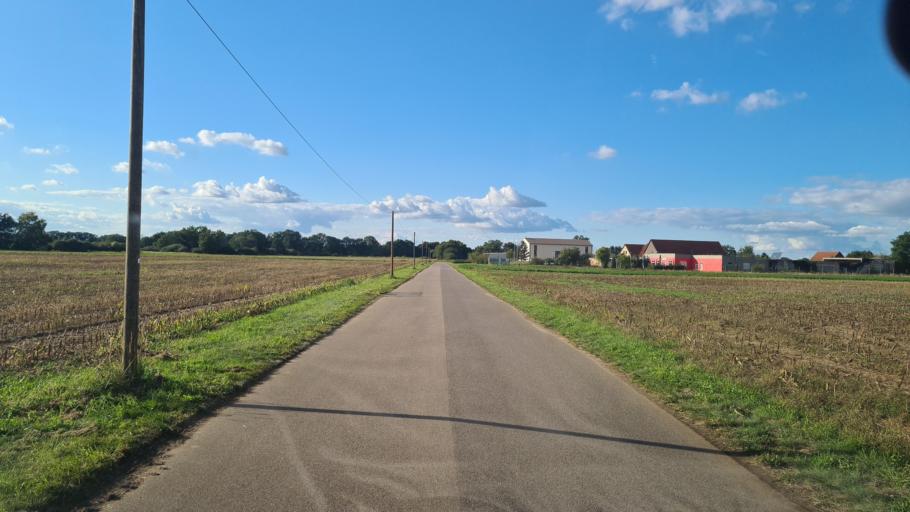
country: DE
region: Brandenburg
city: Herzberg
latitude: 51.7089
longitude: 13.2224
